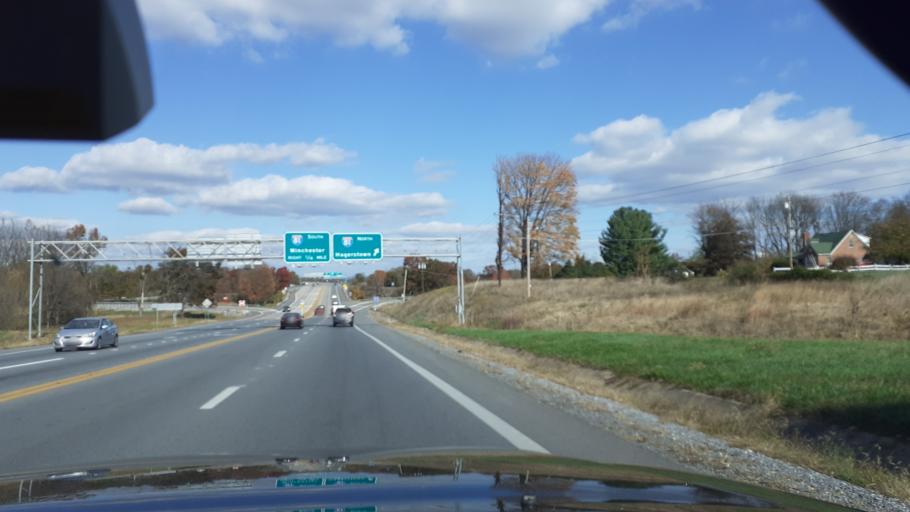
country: US
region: West Virginia
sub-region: Berkeley County
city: Martinsburg
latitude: 39.4911
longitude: -77.9584
